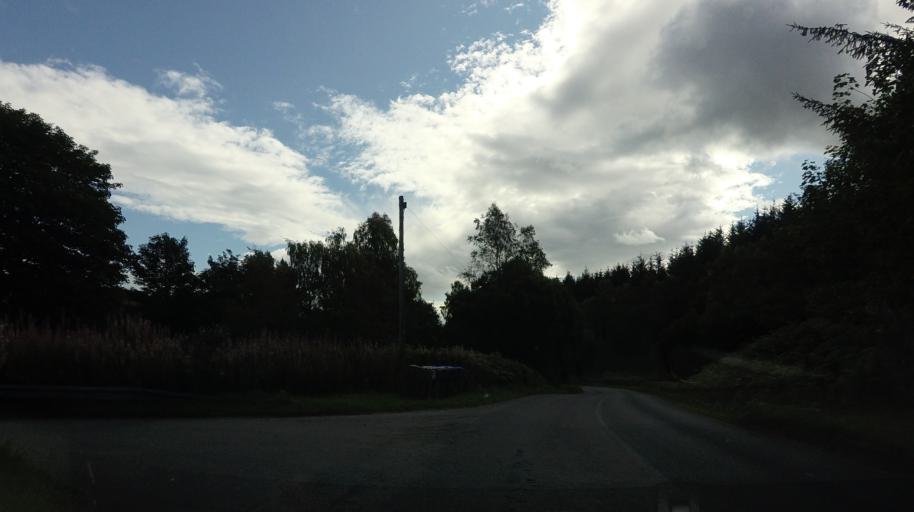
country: GB
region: Scotland
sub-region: Aberdeenshire
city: Torphins
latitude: 57.1241
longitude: -2.6687
